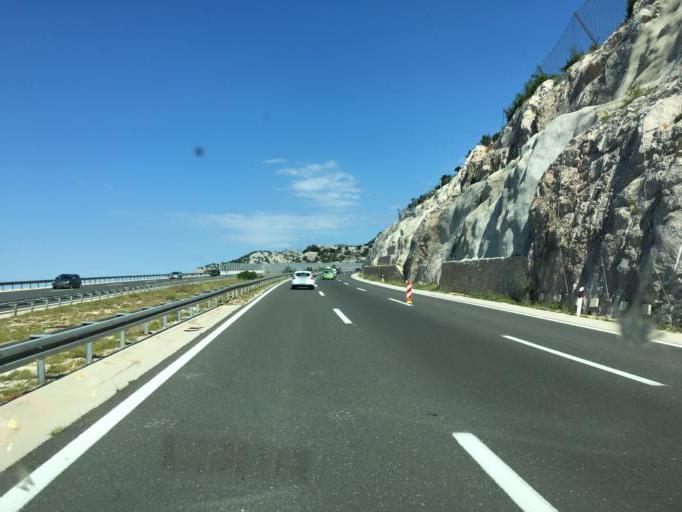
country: HR
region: Zadarska
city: Krusevo
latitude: 44.2486
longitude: 15.6063
